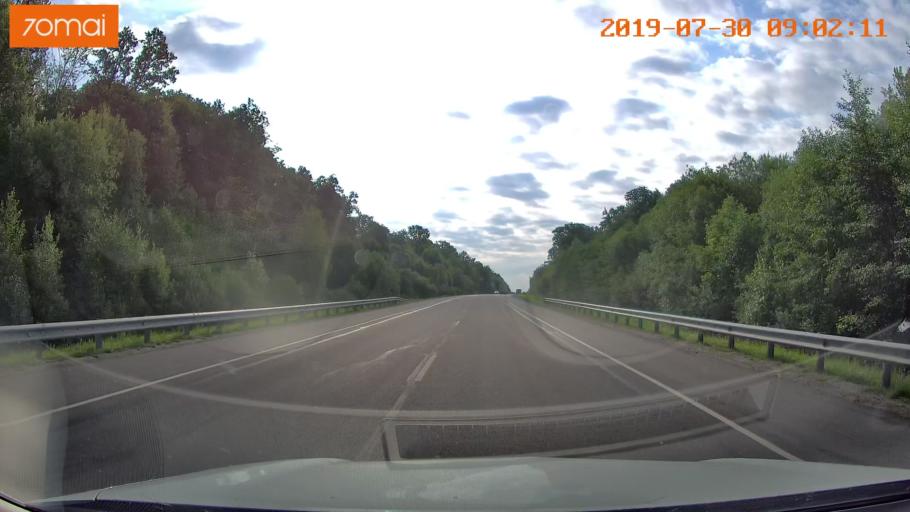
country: RU
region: Kaliningrad
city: Gusev
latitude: 54.6172
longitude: 22.2257
